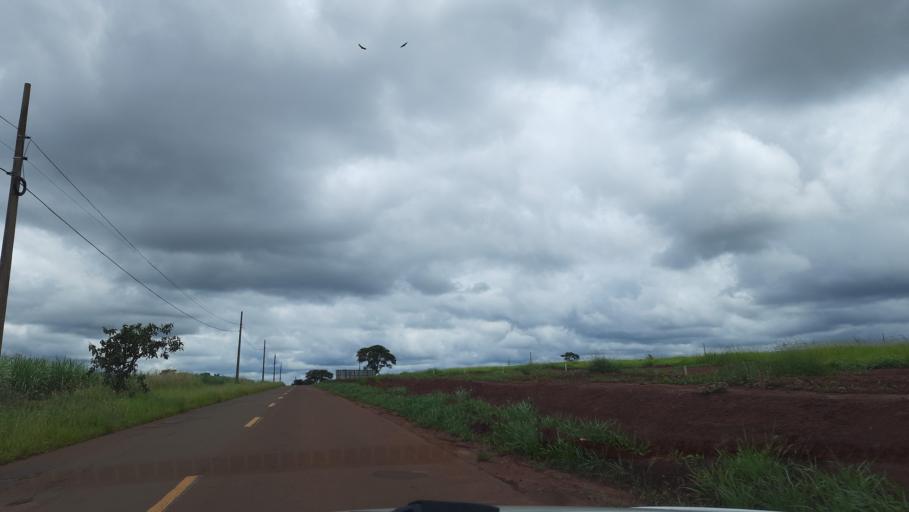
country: BR
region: Sao Paulo
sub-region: Casa Branca
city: Casa Branca
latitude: -21.7955
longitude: -47.0976
